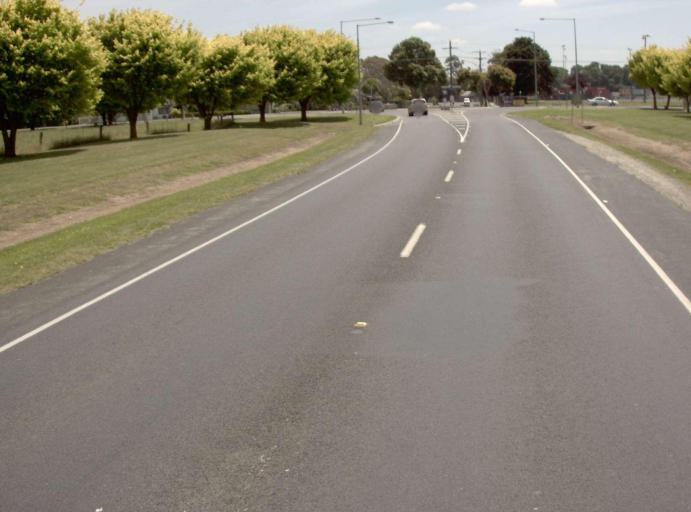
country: AU
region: Victoria
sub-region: Latrobe
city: Traralgon
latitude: -38.2027
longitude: 146.5445
